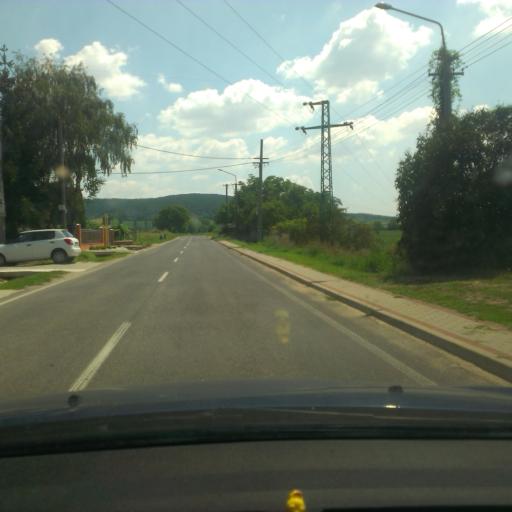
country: SK
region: Trnavsky
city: Hlohovec
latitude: 48.4705
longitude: 17.8104
